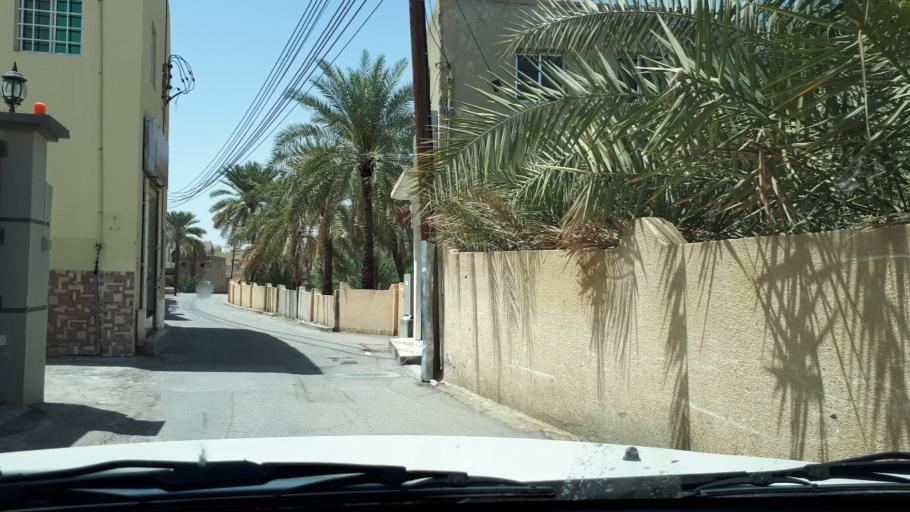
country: OM
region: Muhafazat ad Dakhiliyah
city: Nizwa
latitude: 22.9280
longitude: 57.5318
